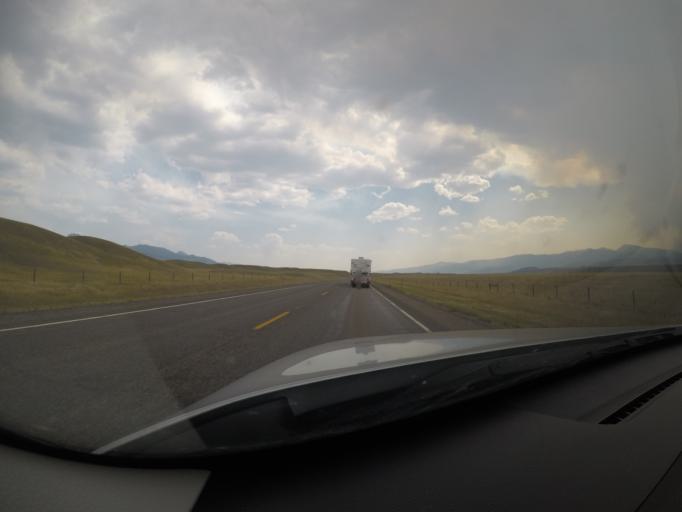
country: US
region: Montana
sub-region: Gallatin County
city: Big Sky
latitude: 45.0985
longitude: -111.6488
